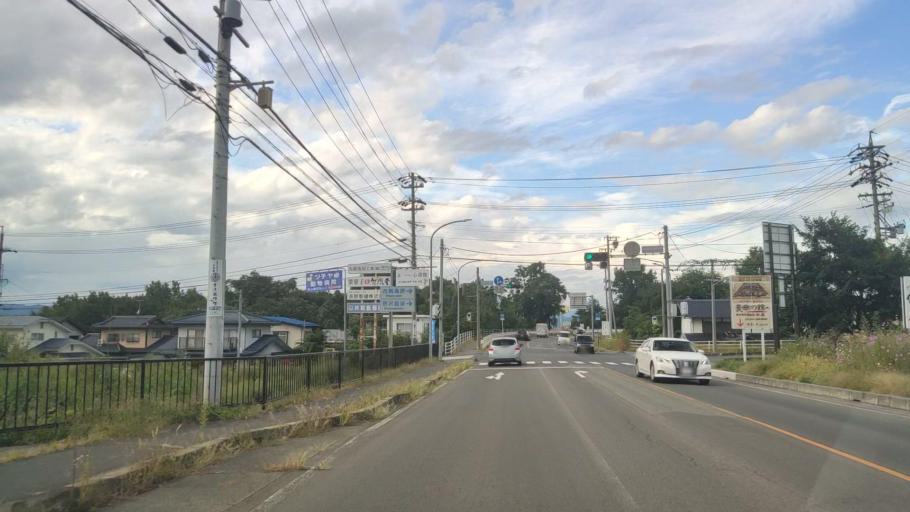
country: JP
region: Nagano
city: Suzaka
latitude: 36.6864
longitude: 138.3156
